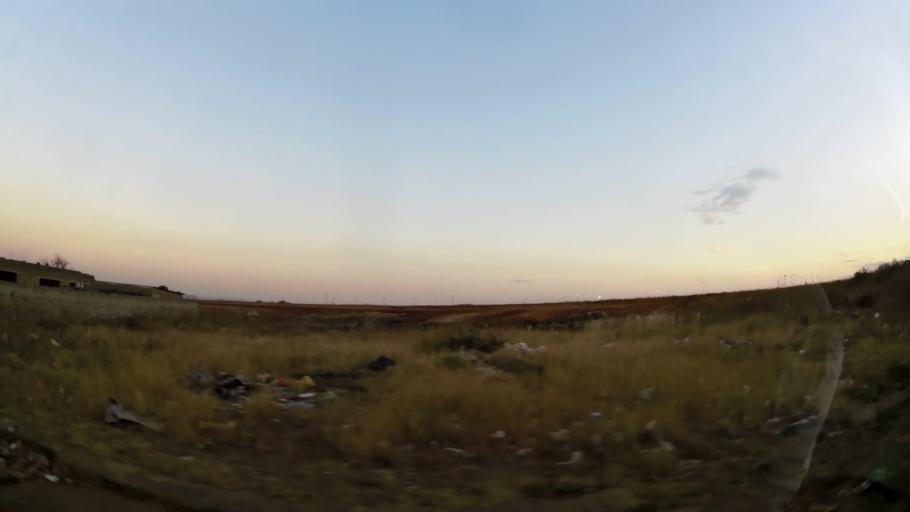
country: ZA
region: Gauteng
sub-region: West Rand District Municipality
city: Randfontein
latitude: -26.2123
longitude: 27.7105
